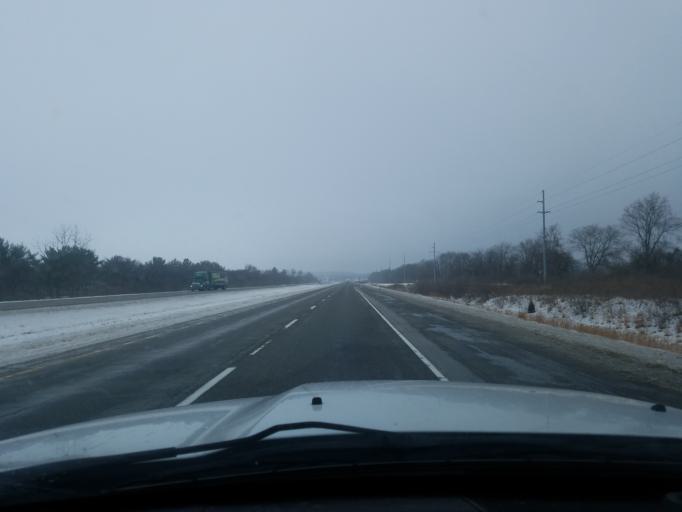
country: US
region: Indiana
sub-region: Fulton County
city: Rochester
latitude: 41.0226
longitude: -86.1769
